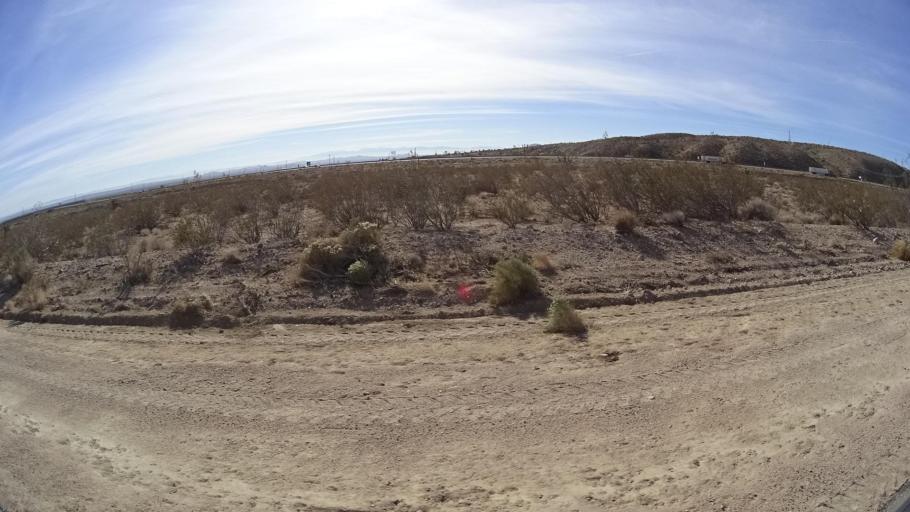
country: US
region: California
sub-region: Kern County
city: Mojave
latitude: 35.1189
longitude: -118.1972
